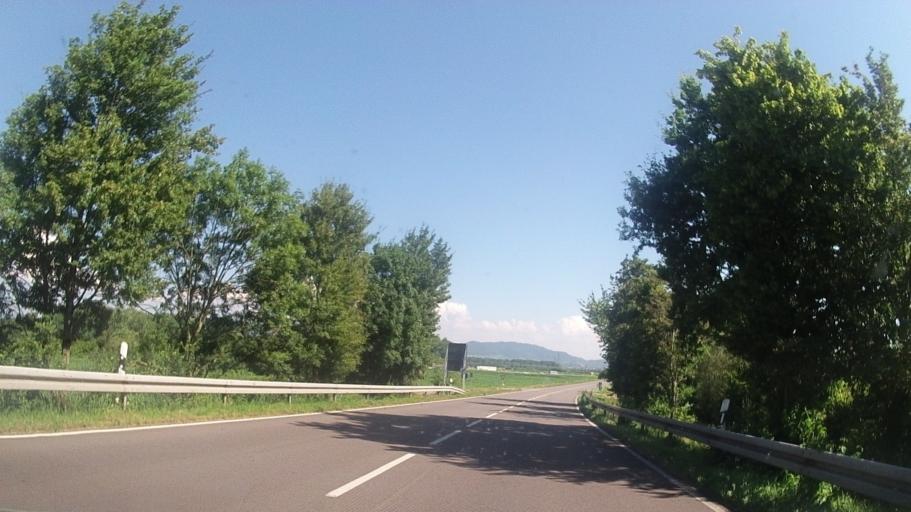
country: DE
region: Baden-Wuerttemberg
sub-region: Freiburg Region
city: Willstatt
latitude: 48.5322
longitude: 7.9240
